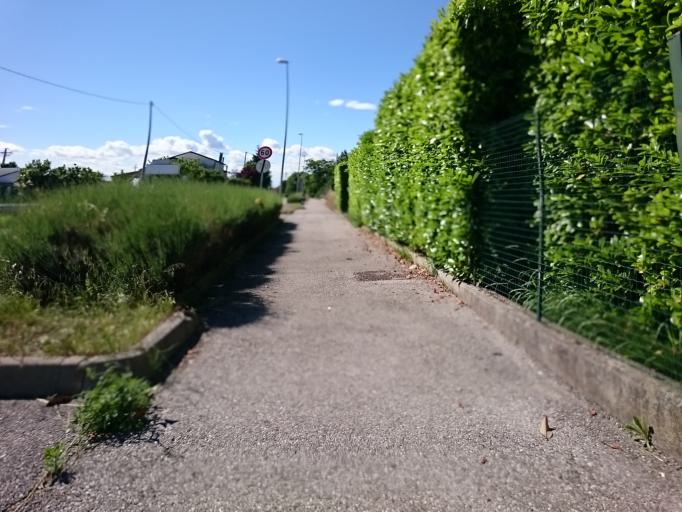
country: IT
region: Veneto
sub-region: Provincia di Venezia
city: Campolongo Maggiore
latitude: 45.3217
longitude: 12.0301
